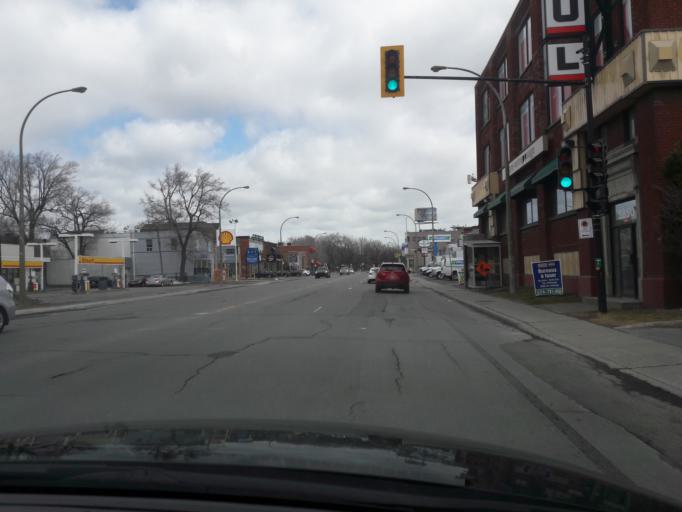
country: CA
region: Quebec
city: Mont-Royal
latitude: 45.5038
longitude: -73.6435
